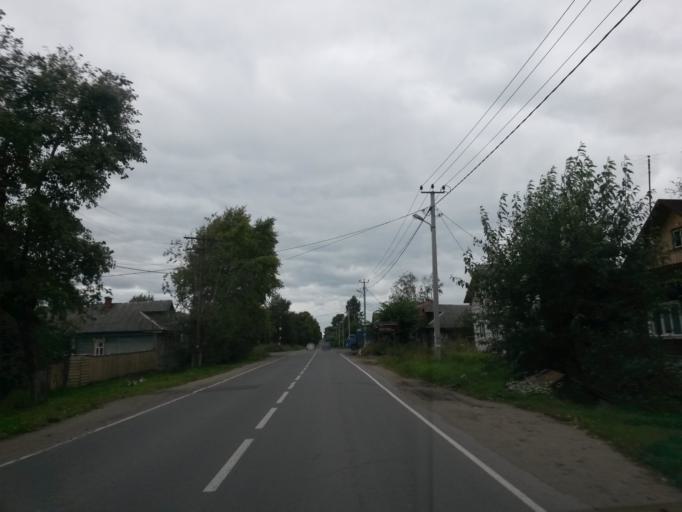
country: RU
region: Jaroslavl
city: Tutayev
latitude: 57.8801
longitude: 39.5559
